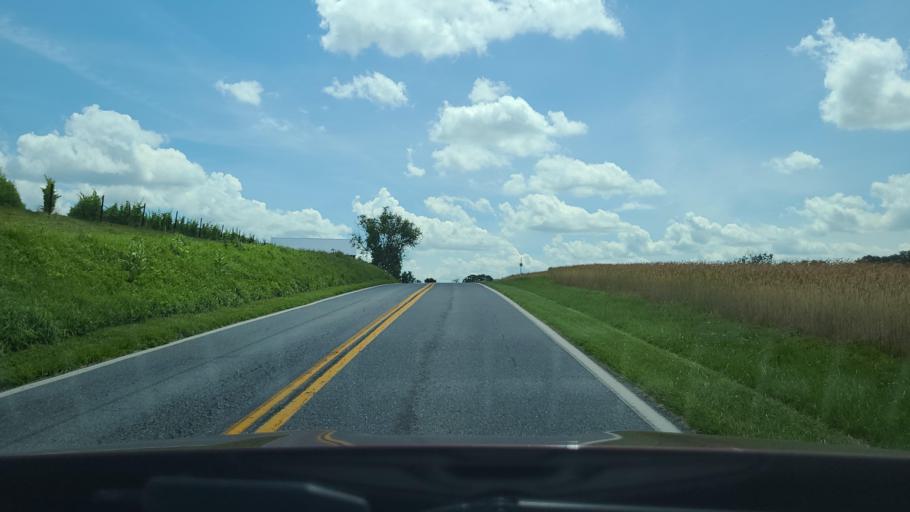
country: US
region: Maryland
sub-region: Montgomery County
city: Clarksburg
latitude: 39.2687
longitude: -77.2529
